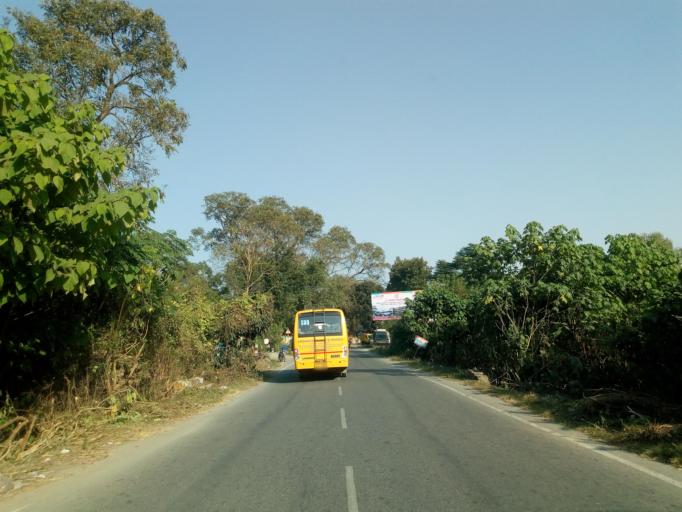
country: IN
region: Uttarakhand
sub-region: Dehradun
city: Dehradun
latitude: 30.3443
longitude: 77.9148
